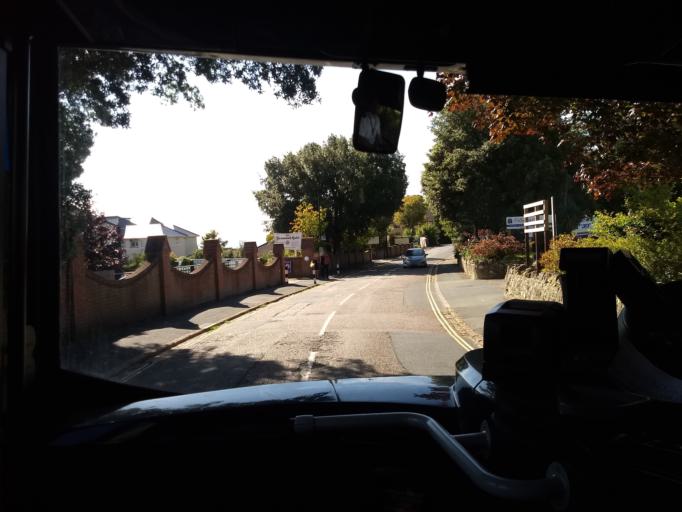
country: GB
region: England
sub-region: Isle of Wight
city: Shanklin
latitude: 50.6283
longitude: -1.1751
